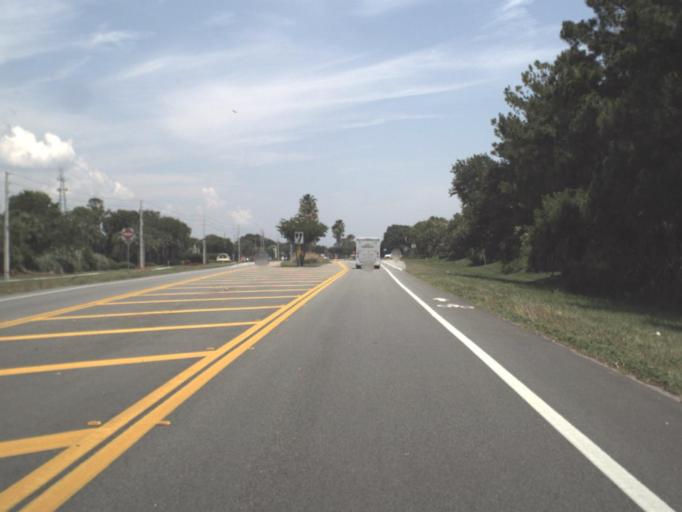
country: US
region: Florida
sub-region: Saint Johns County
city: Sawgrass
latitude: 30.1853
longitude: -81.3791
